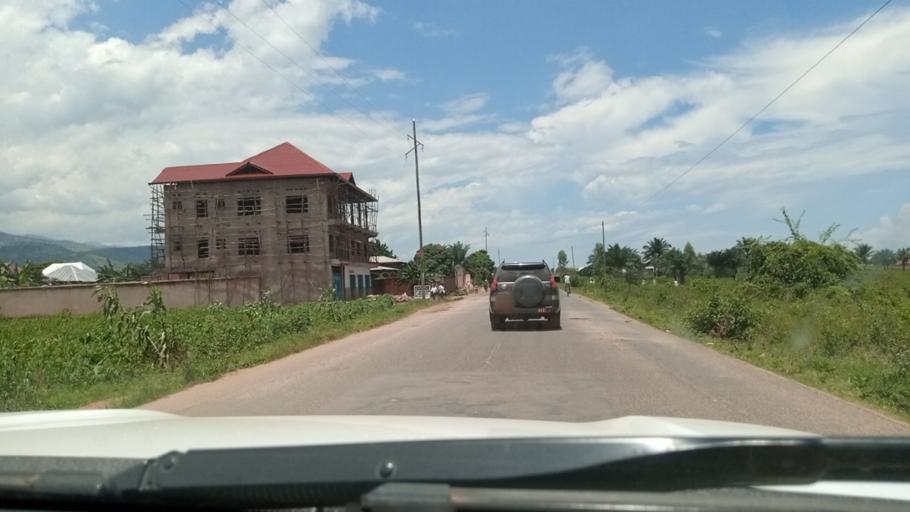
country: BI
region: Bujumbura Mairie
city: Bujumbura
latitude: -3.4632
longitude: 29.3504
